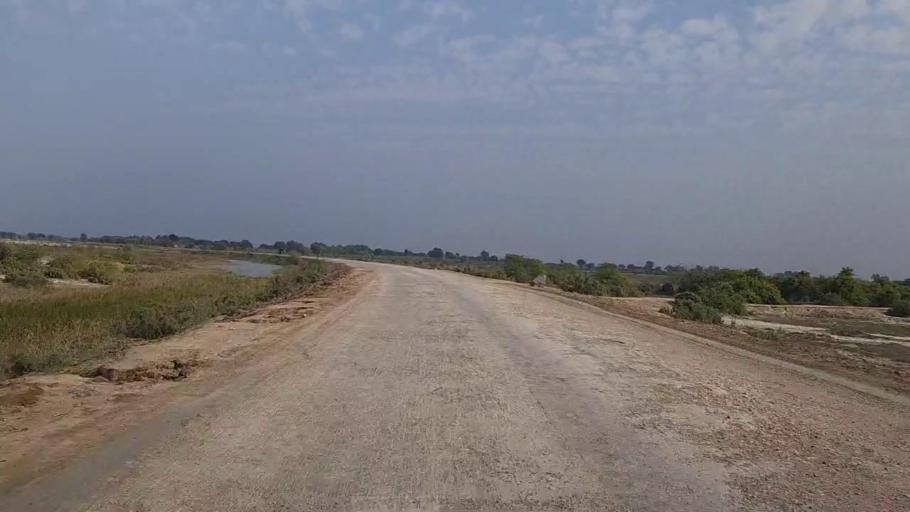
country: PK
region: Sindh
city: Mirwah Gorchani
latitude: 25.4044
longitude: 69.0483
